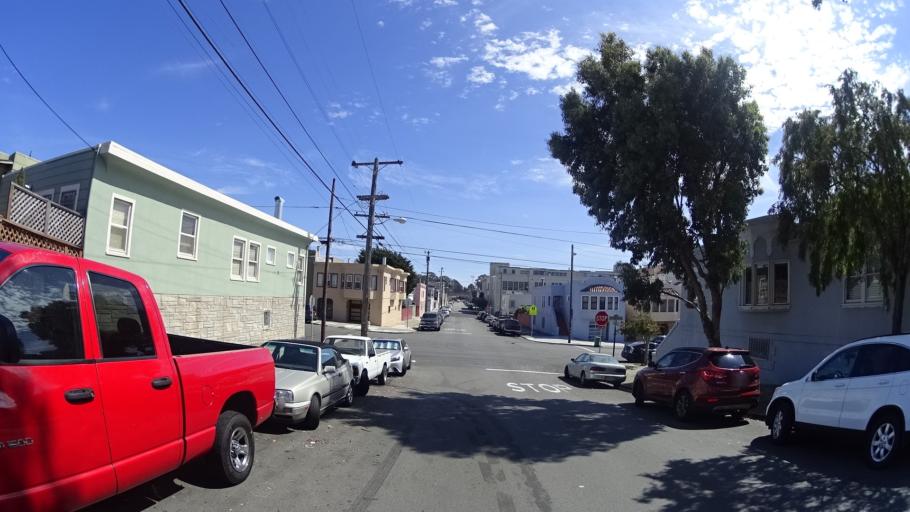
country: US
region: California
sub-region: San Mateo County
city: Daly City
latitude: 37.7167
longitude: -122.4358
